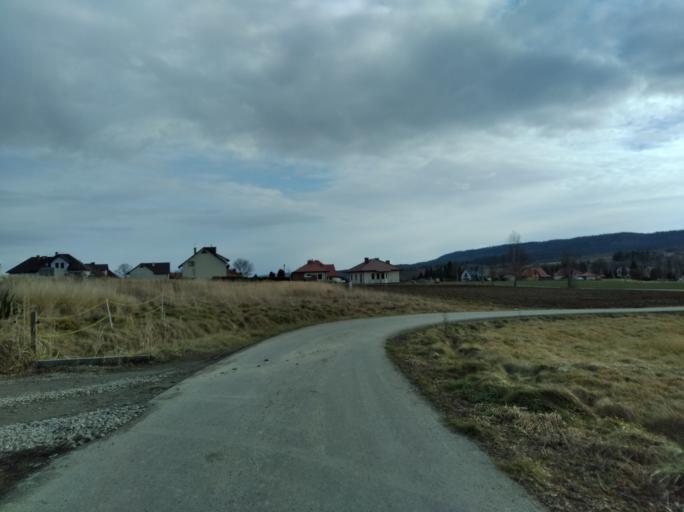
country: PL
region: Subcarpathian Voivodeship
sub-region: Powiat strzyzowski
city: Strzyzow
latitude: 49.8514
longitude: 21.7743
